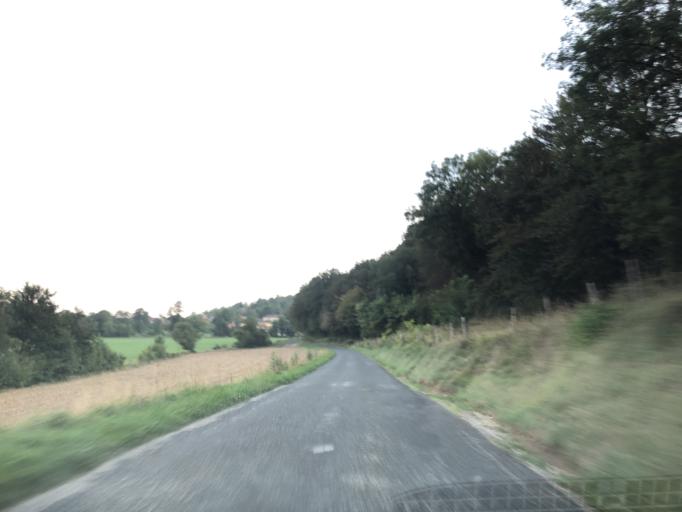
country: FR
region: Rhone-Alpes
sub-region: Departement de l'Ain
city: Belley
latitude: 45.7851
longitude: 5.6262
